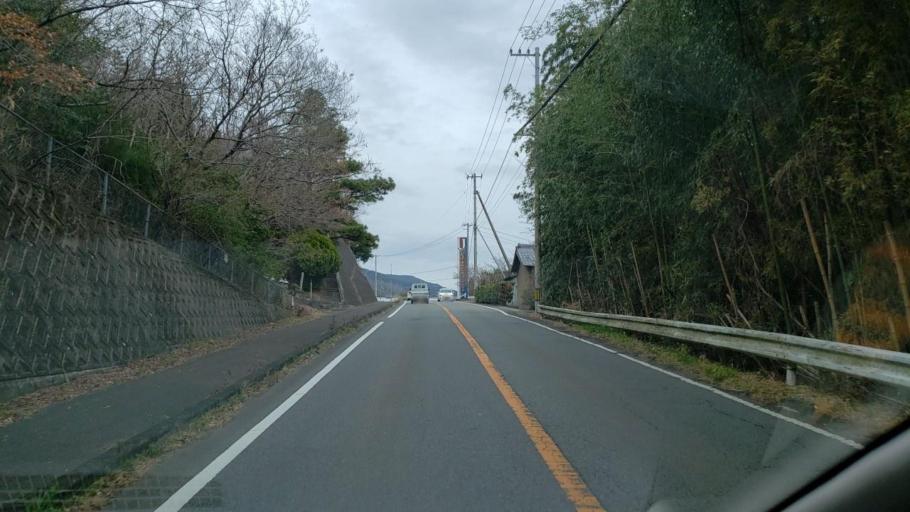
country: JP
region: Tokushima
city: Kamojimacho-jogejima
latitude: 34.1200
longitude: 134.3428
